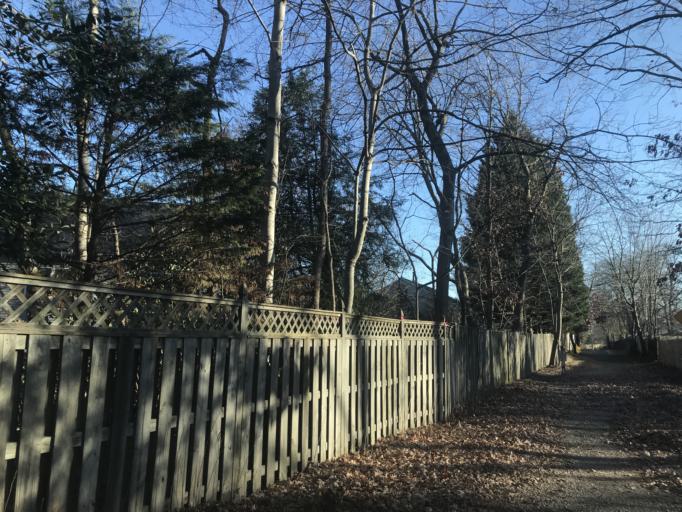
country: US
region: Virginia
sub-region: Fairfax County
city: Franconia
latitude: 38.7886
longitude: -77.1486
